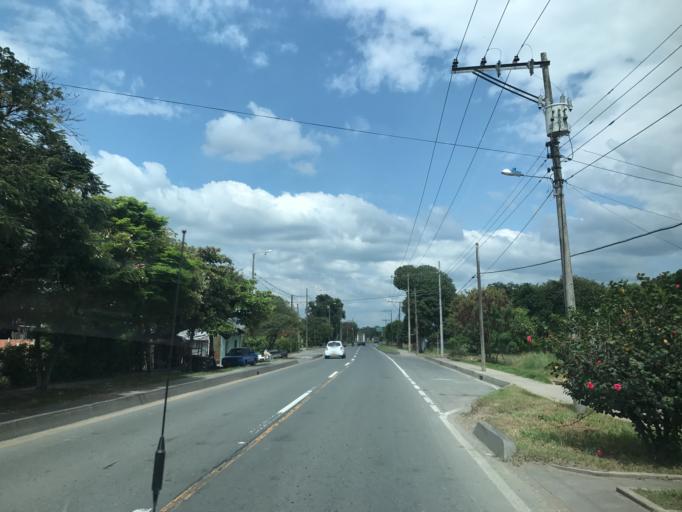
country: CO
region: Valle del Cauca
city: Obando
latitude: 4.5793
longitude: -75.9733
